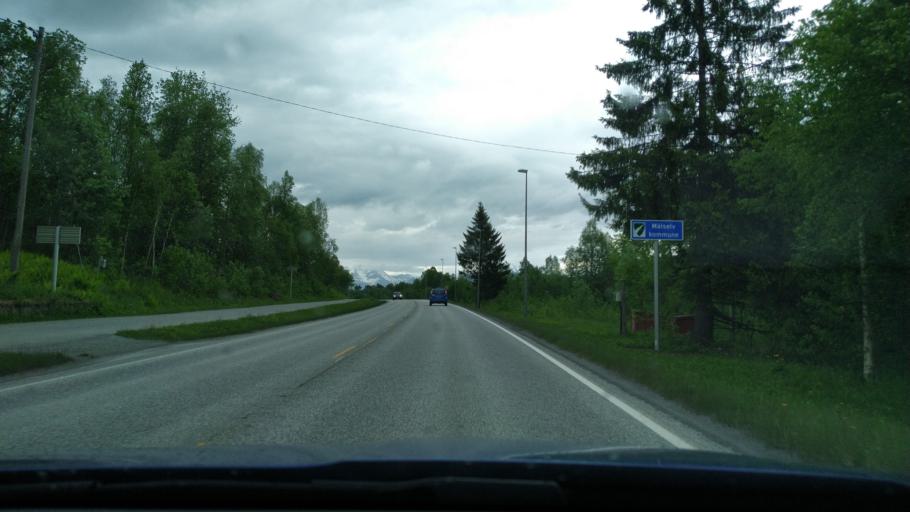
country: NO
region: Troms
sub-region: Malselv
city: Moen
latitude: 69.0252
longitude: 18.4968
